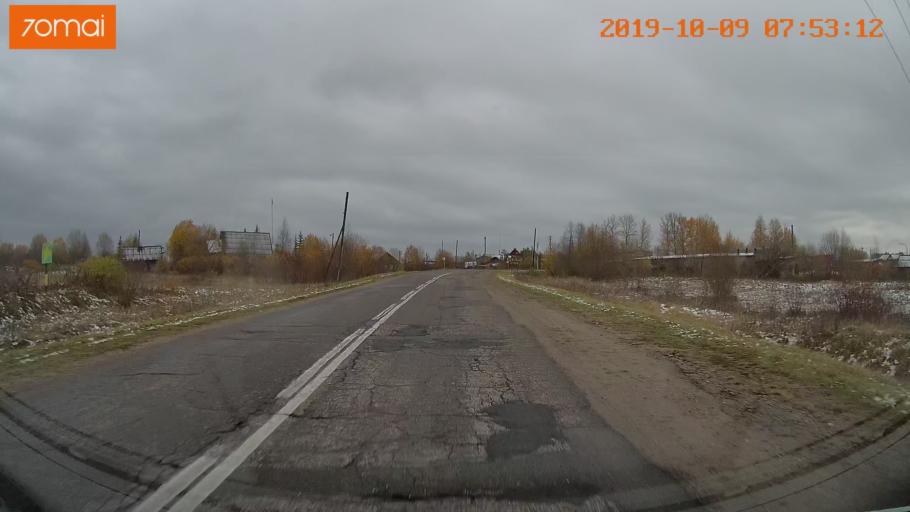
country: RU
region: Jaroslavl
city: Kukoboy
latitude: 58.6970
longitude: 39.8931
